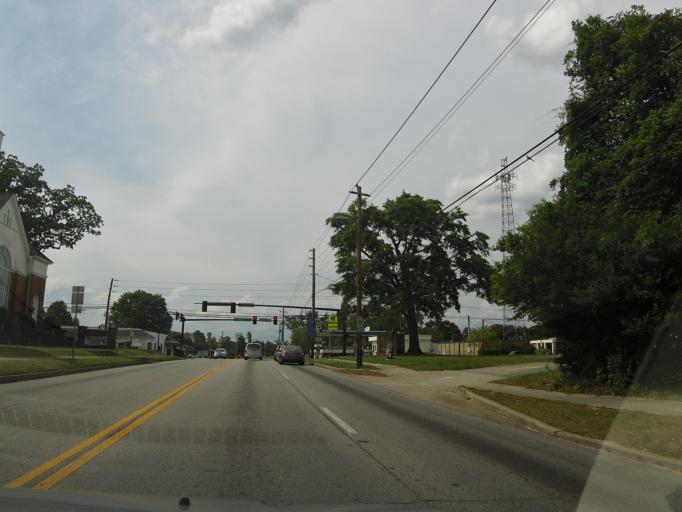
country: US
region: Georgia
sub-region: McDuffie County
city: Thomson
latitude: 33.4699
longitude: -82.5045
